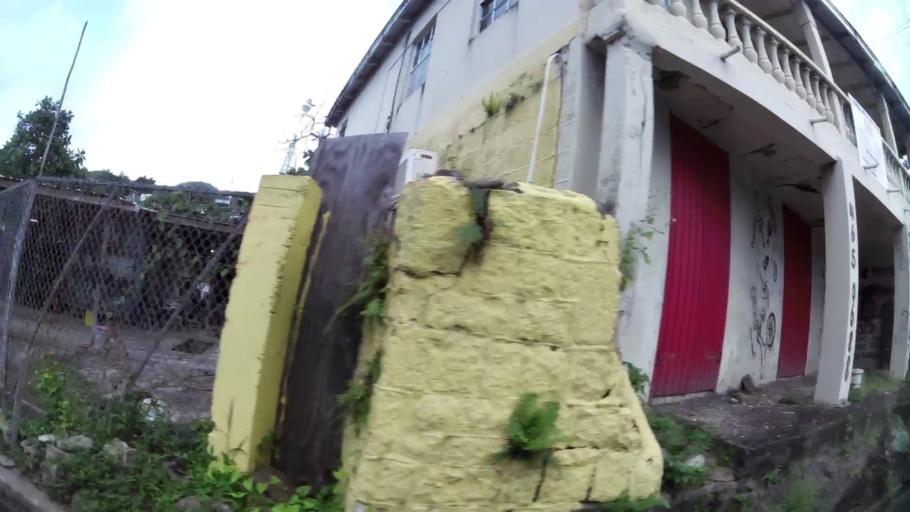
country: KN
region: Saint Mary Cayon
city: Cayon
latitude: 17.3500
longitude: -62.7305
